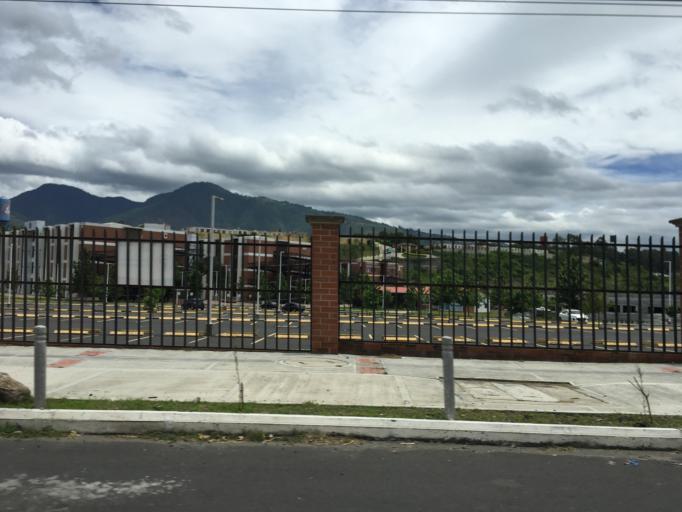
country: GT
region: Guatemala
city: Amatitlan
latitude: 14.5030
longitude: -90.6129
